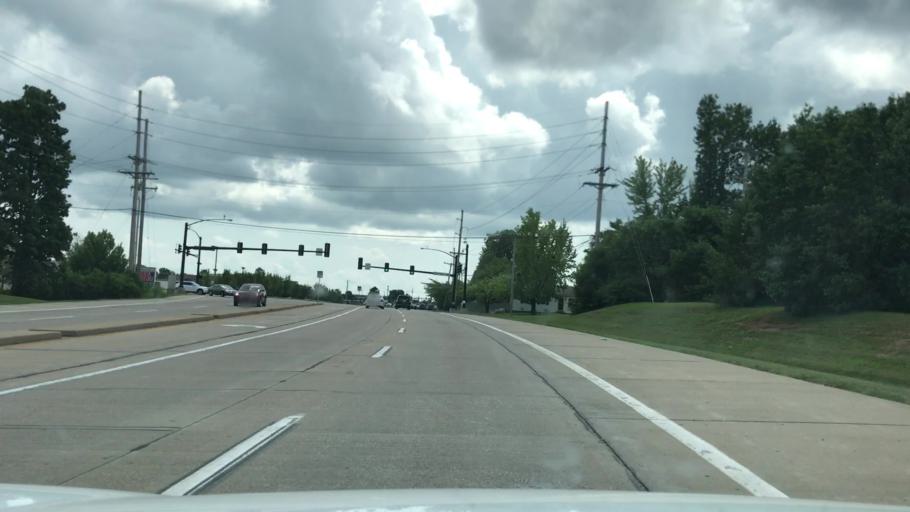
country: US
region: Missouri
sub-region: Saint Charles County
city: O'Fallon
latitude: 38.7882
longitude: -90.7000
